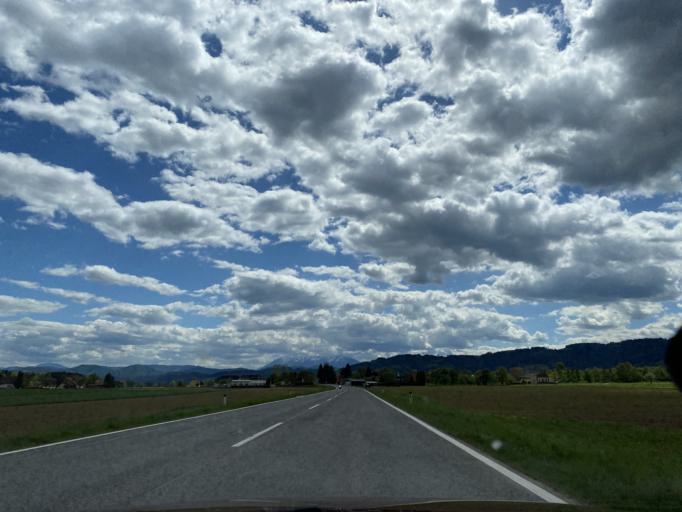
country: AT
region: Carinthia
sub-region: Politischer Bezirk Wolfsberg
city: Sankt Andrae
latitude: 46.7953
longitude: 14.8266
